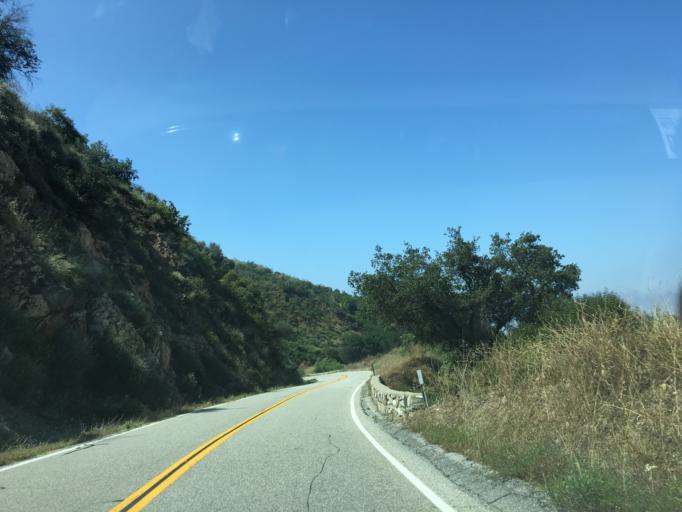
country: US
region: California
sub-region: Los Angeles County
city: Glendora
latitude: 34.1888
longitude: -117.8413
